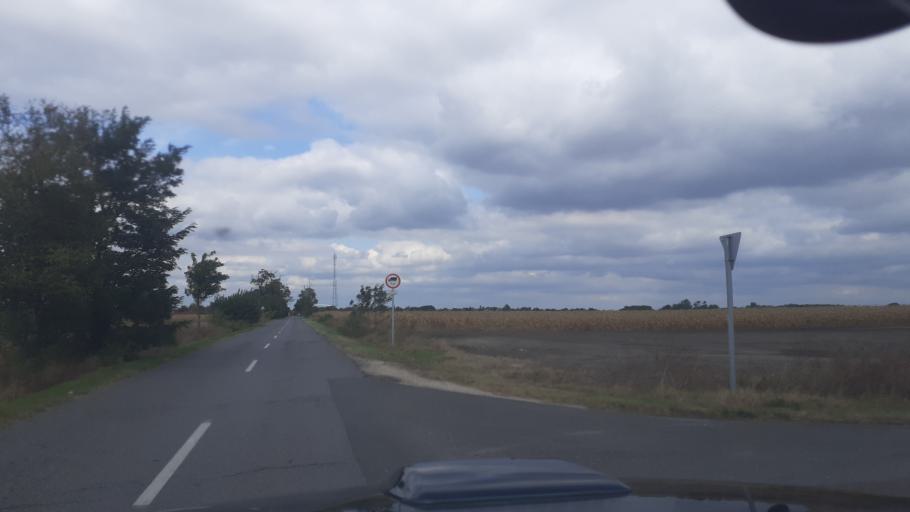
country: HU
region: Bacs-Kiskun
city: Apostag
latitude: 46.8648
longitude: 18.9558
